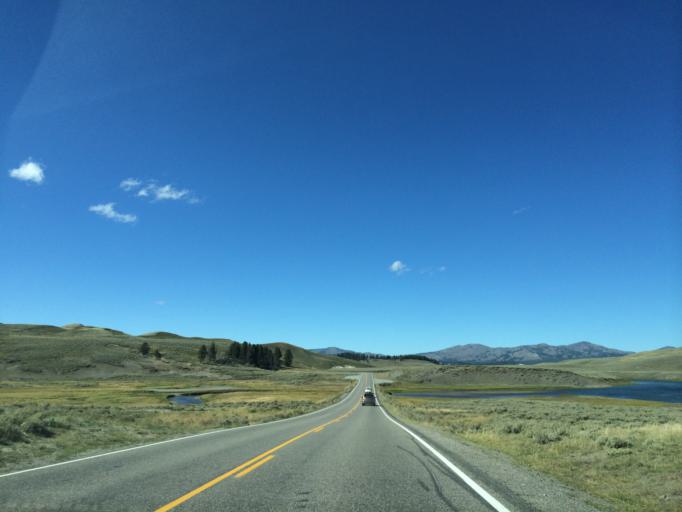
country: US
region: Montana
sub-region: Gallatin County
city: West Yellowstone
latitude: 44.6441
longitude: -110.4576
